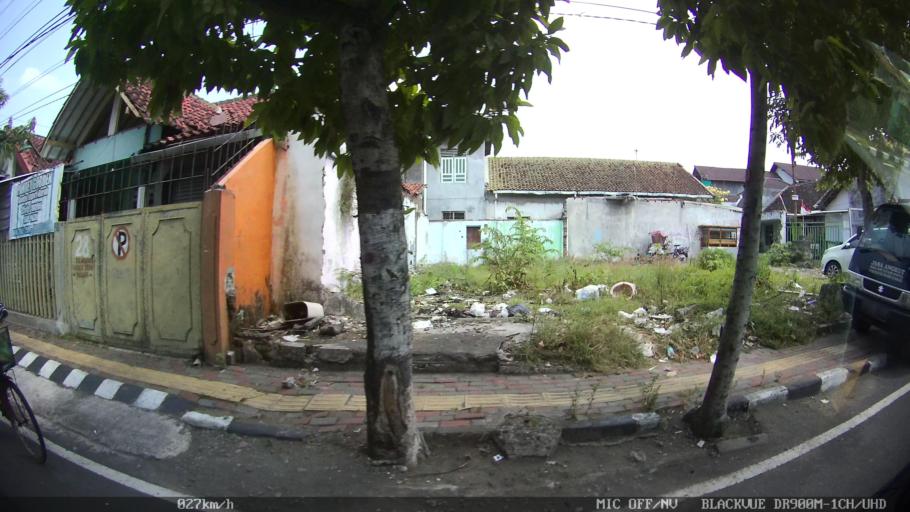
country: ID
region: Daerah Istimewa Yogyakarta
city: Yogyakarta
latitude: -7.8146
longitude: 110.3863
